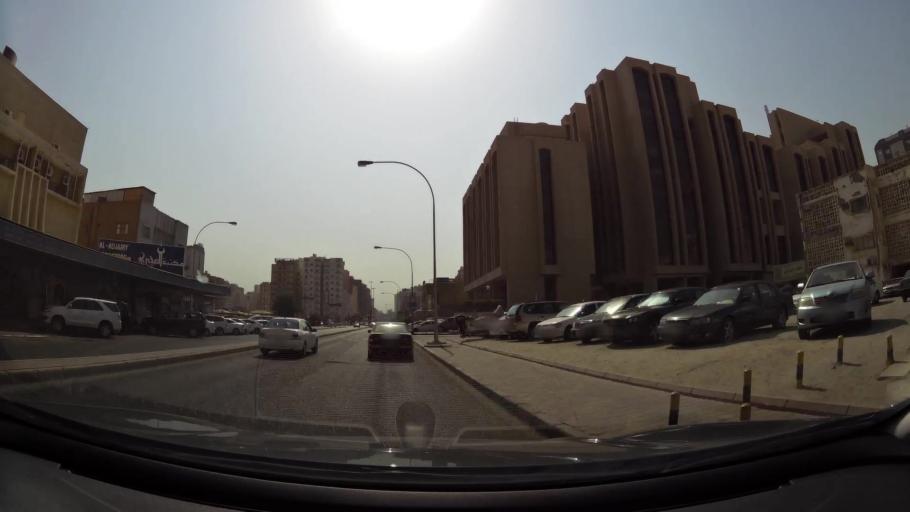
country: KW
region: Muhafazat Hawalli
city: Hawalli
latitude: 29.3338
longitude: 48.0085
